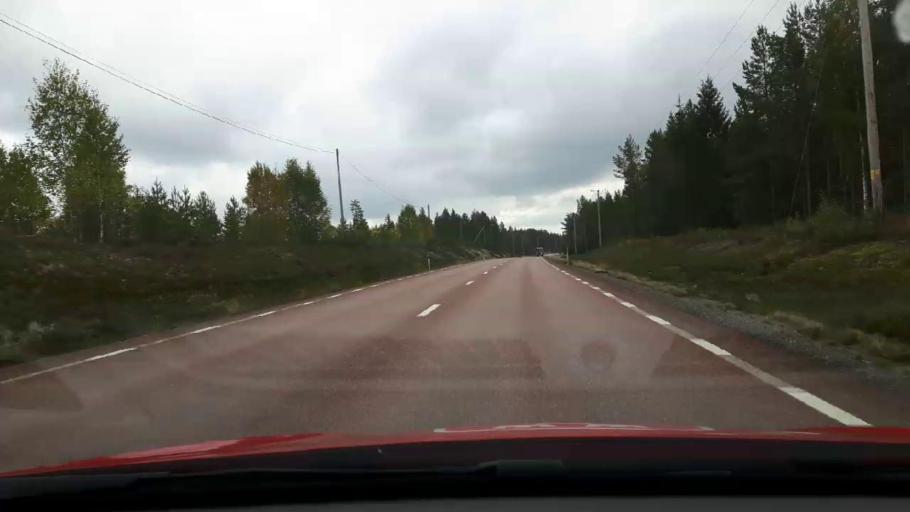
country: SE
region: Gaevleborg
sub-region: Soderhamns Kommun
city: Soderhamn
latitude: 61.1348
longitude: 16.9177
